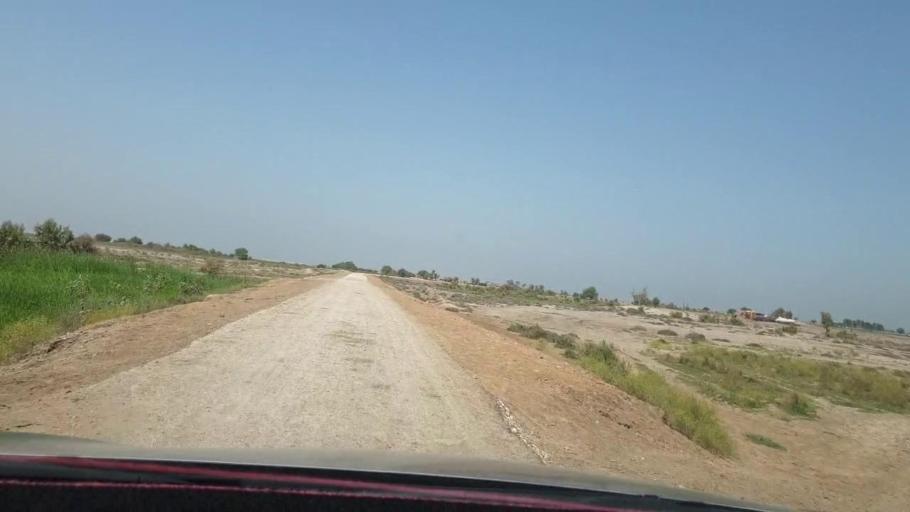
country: PK
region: Sindh
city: Warah
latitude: 27.5204
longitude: 67.7086
